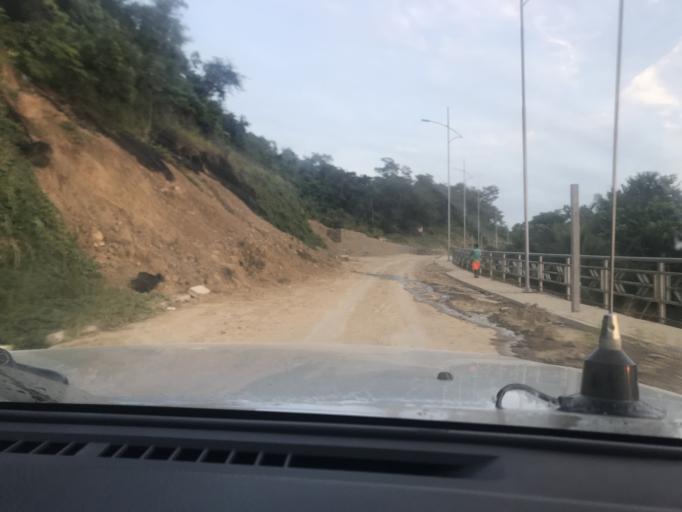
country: BO
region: El Beni
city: Rurrenabaque
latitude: -14.4420
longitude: -67.5356
